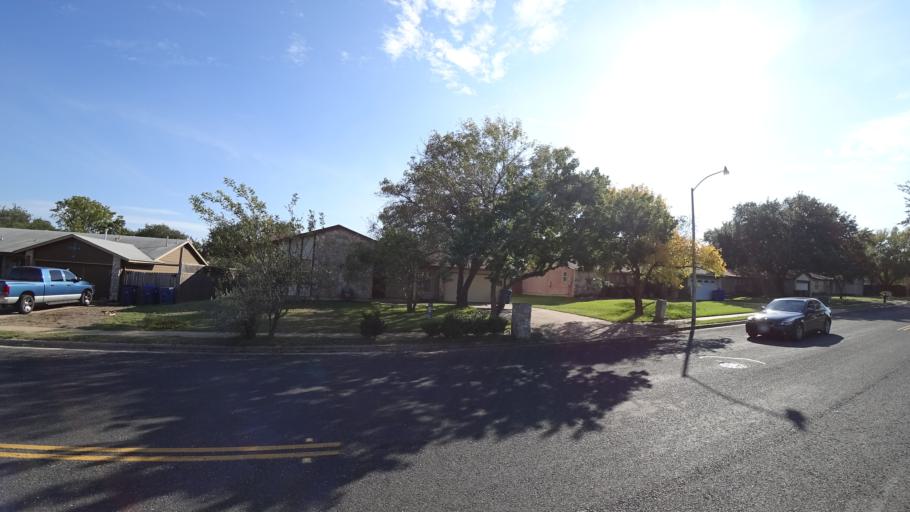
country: US
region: Texas
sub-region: Williamson County
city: Anderson Mill
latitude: 30.4544
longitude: -97.8132
